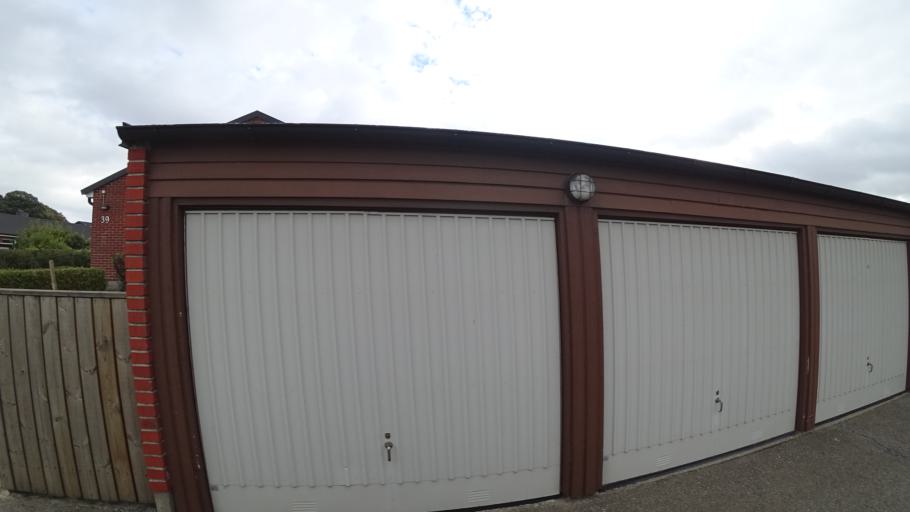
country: SE
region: Skane
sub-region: Kavlinge Kommun
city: Kaevlinge
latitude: 55.7718
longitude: 13.0914
